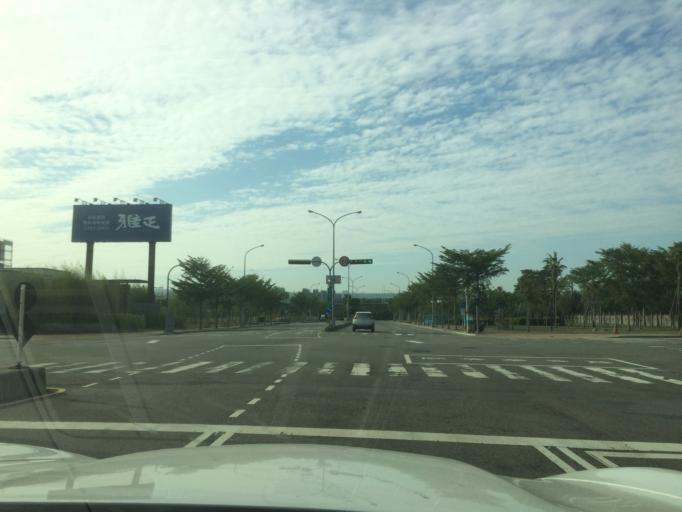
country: TW
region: Taiwan
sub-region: Taichung City
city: Taichung
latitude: 24.1518
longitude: 120.6269
